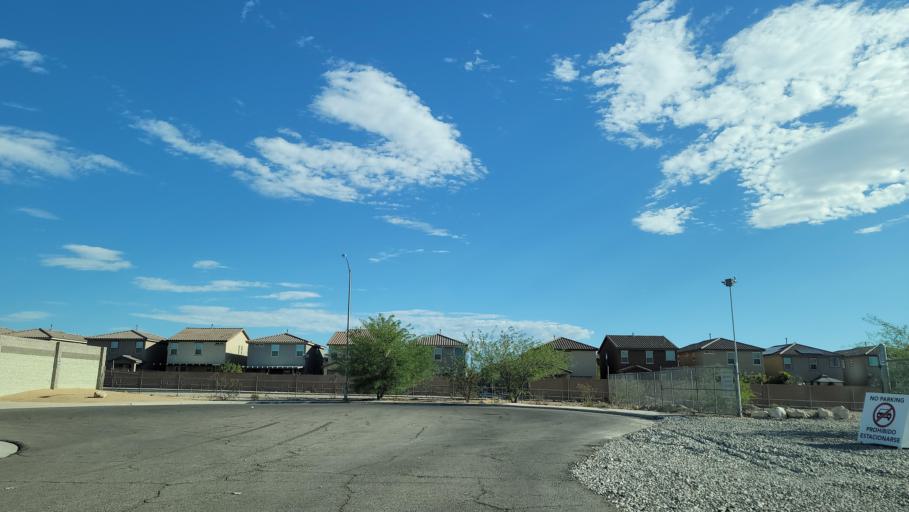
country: US
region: Nevada
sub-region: Clark County
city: Spring Valley
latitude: 36.0865
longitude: -115.2815
